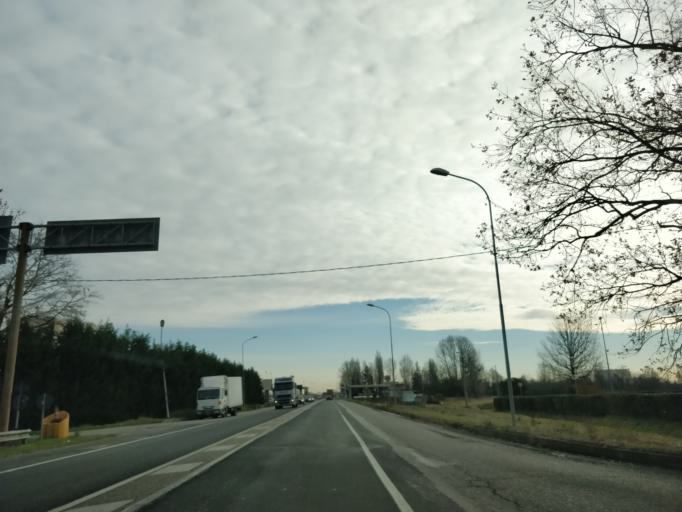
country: IT
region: Emilia-Romagna
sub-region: Provincia di Bologna
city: Castel Maggiore
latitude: 44.5943
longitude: 11.3809
